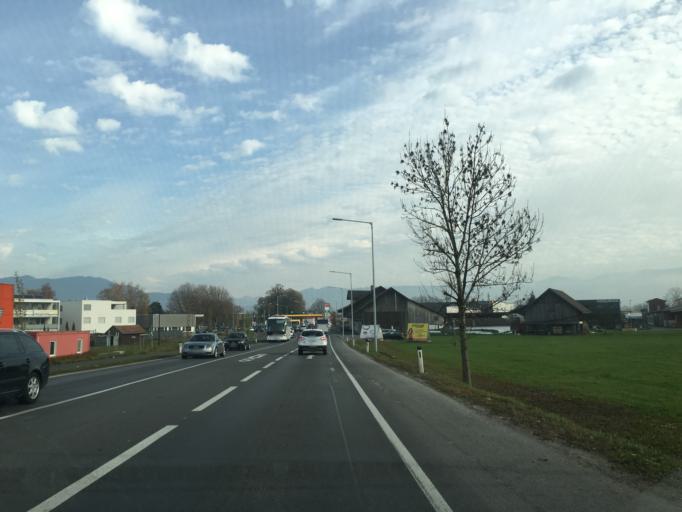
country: AT
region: Vorarlberg
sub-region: Politischer Bezirk Bregenz
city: Hard
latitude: 47.4776
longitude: 9.6760
